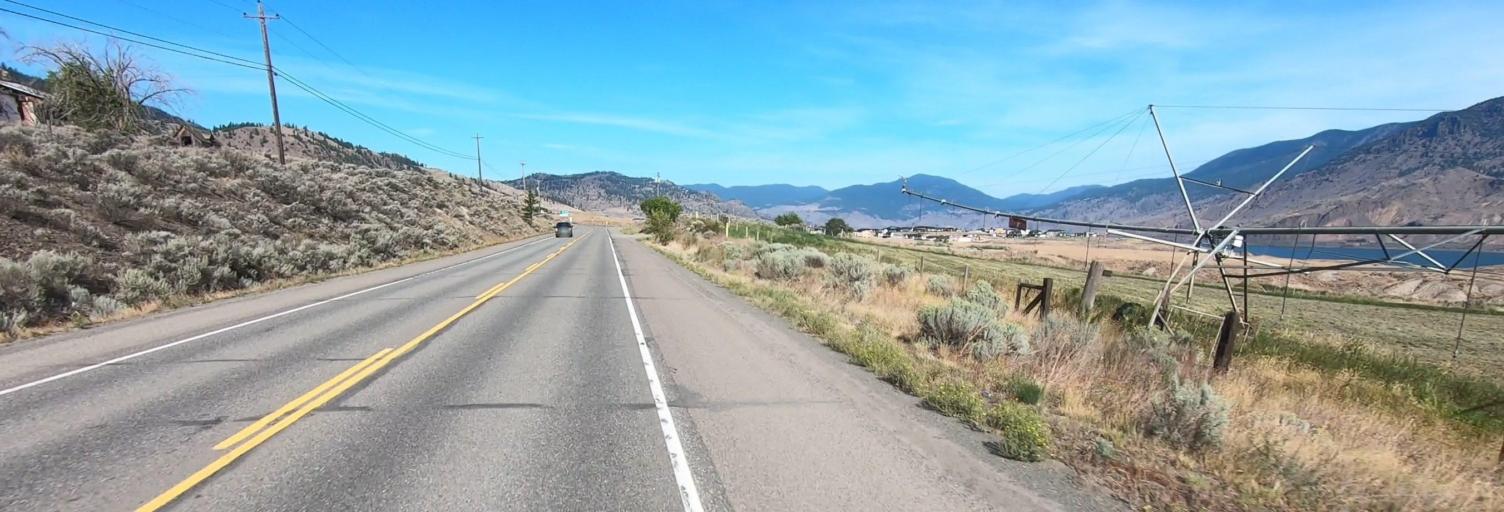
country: CA
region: British Columbia
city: Logan Lake
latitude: 50.7232
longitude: -120.6644
